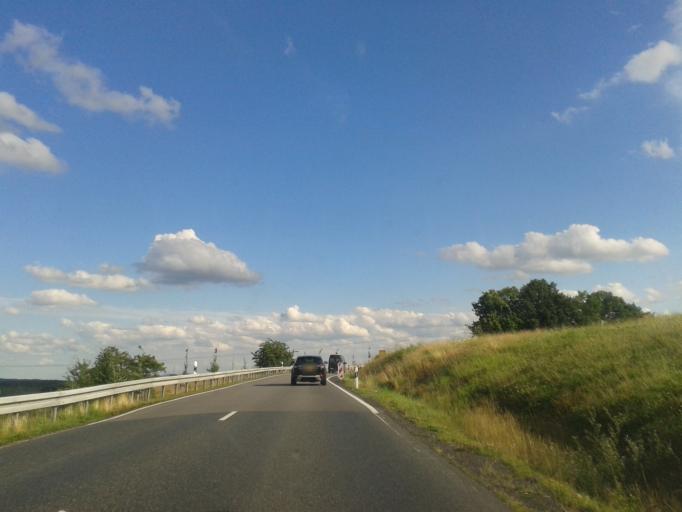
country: DE
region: Saxony
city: Durrrohrsdorf
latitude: 51.0148
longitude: 13.9545
